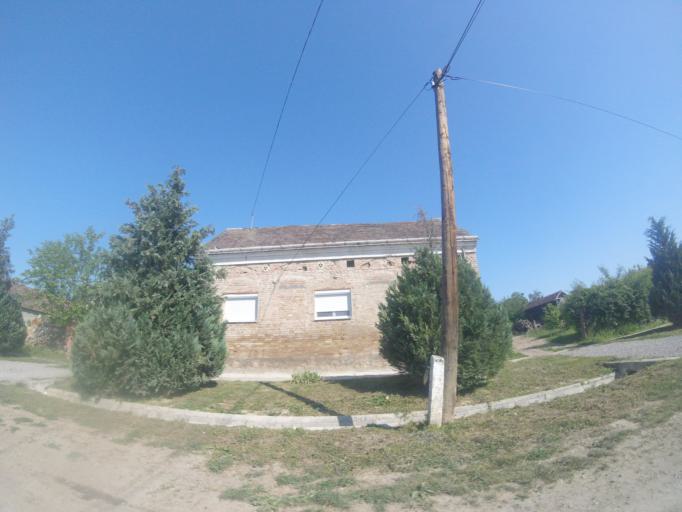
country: HU
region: Baranya
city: Sellye
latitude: 45.9263
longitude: 17.8760
